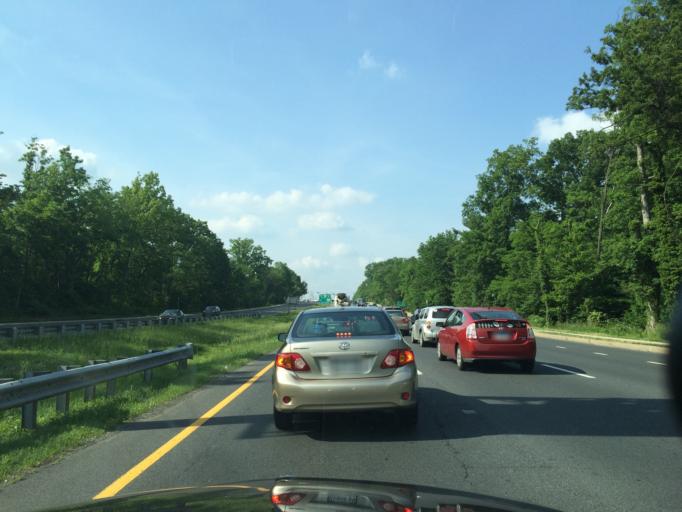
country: US
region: Maryland
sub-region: Montgomery County
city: Rossmoor
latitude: 39.1059
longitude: -77.0764
